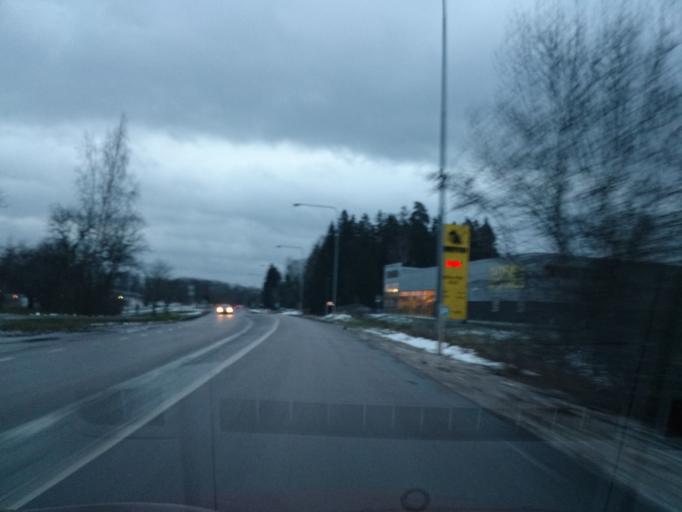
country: SE
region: OEstergoetland
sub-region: Linkopings Kommun
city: Linkoping
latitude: 58.3734
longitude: 15.6684
